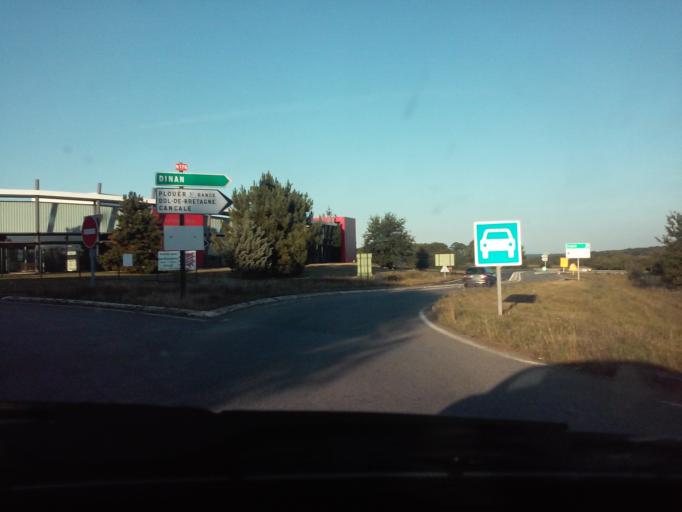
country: FR
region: Brittany
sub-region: Departement des Cotes-d'Armor
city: Pleslin-Trigavou
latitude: 48.5213
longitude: -2.0412
